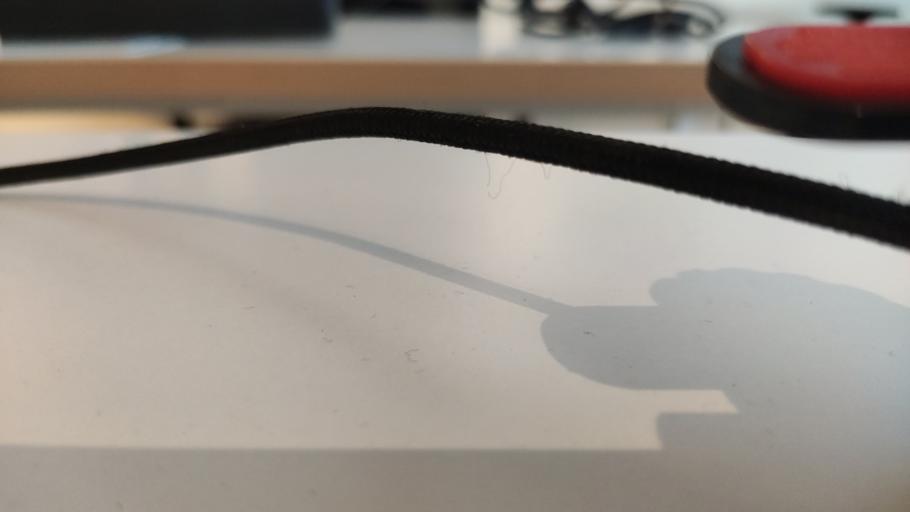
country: RU
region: Moskovskaya
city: Novopetrovskoye
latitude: 55.9505
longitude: 36.4376
